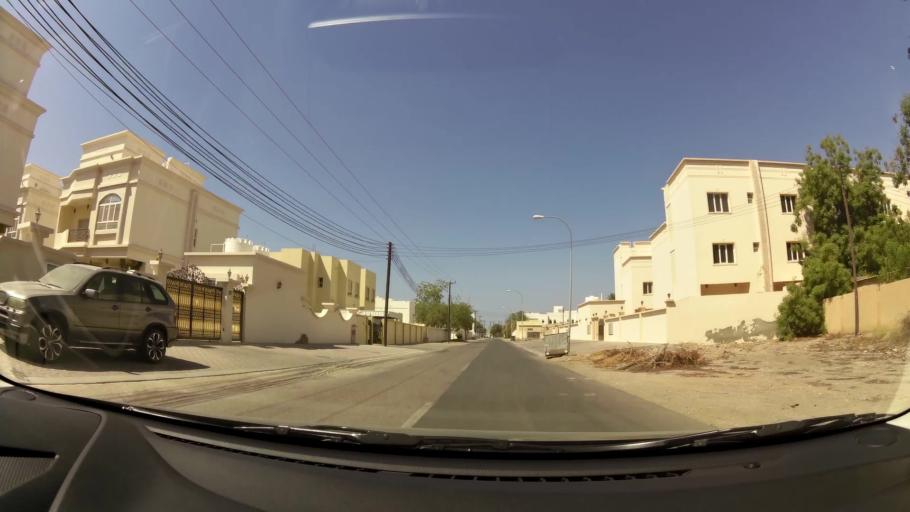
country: OM
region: Muhafazat Masqat
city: As Sib al Jadidah
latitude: 23.6309
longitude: 58.2189
